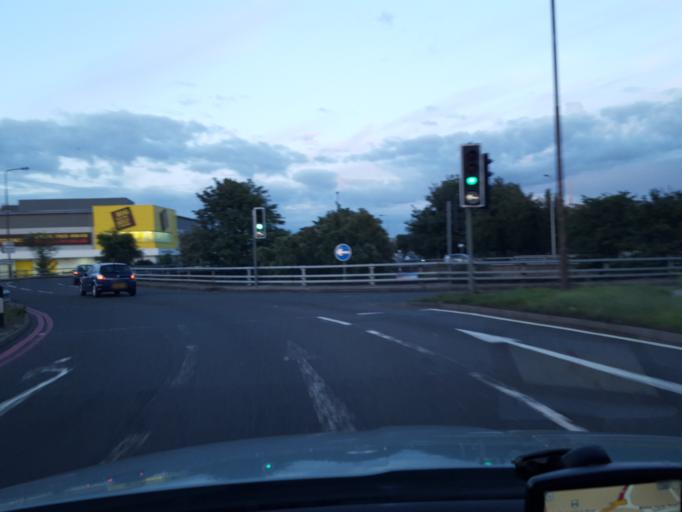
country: GB
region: Scotland
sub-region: Edinburgh
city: Currie
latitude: 55.9221
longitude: -3.2925
